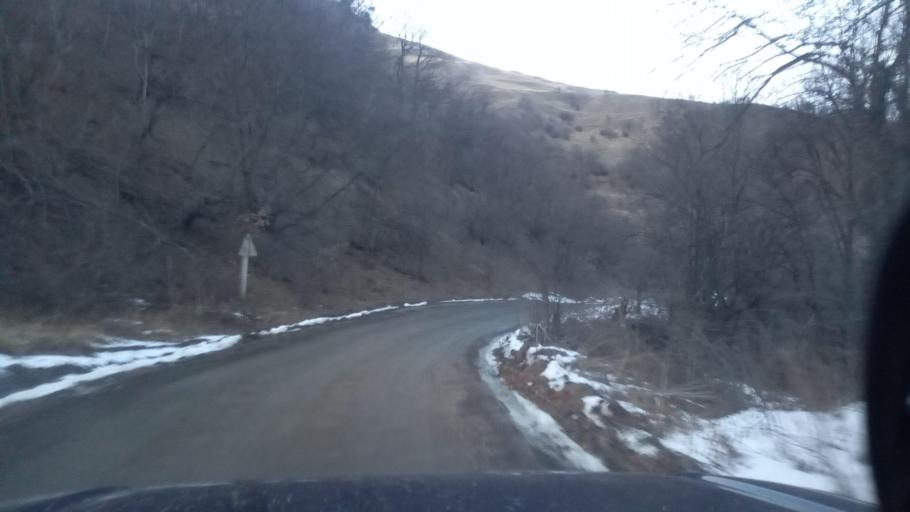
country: RU
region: Ingushetiya
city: Dzhayrakh
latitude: 42.8285
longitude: 44.5852
